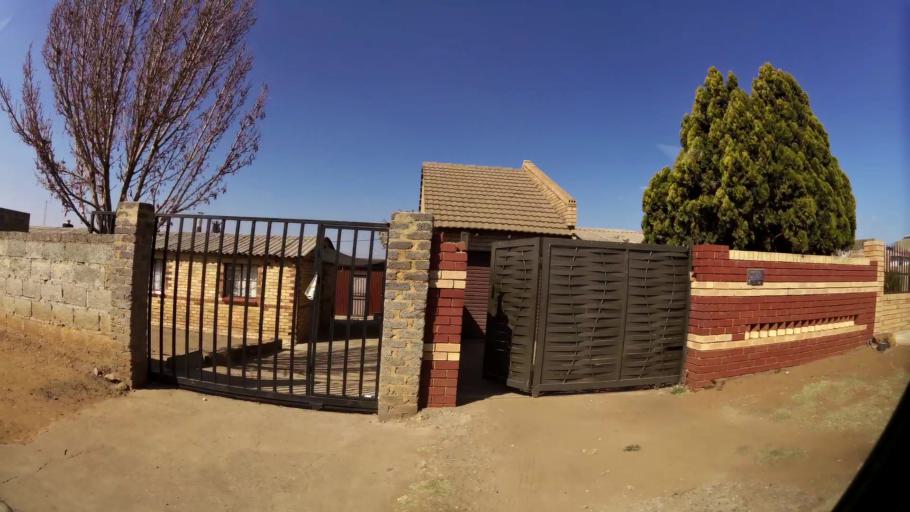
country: ZA
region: Gauteng
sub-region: City of Johannesburg Metropolitan Municipality
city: Soweto
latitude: -26.2319
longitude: 27.8826
